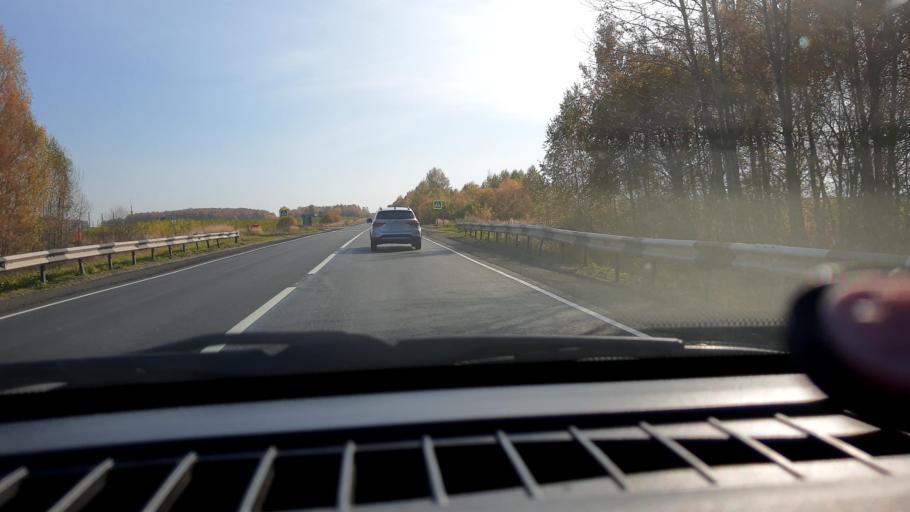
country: RU
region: Nizjnij Novgorod
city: Novaya Balakhna
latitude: 56.5823
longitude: 43.6831
